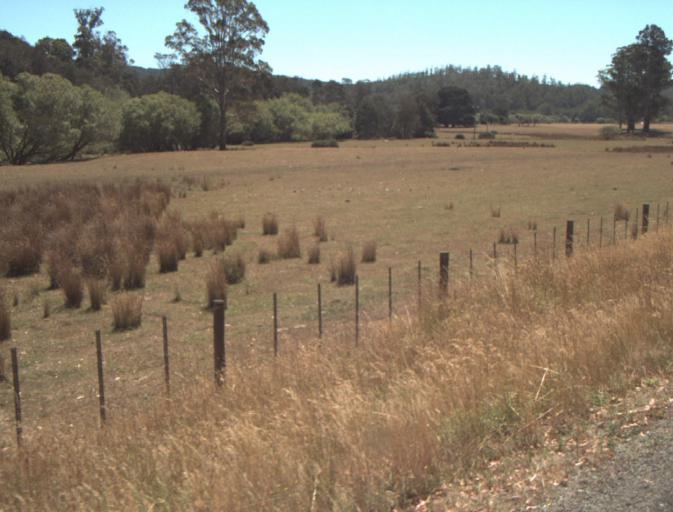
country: AU
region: Tasmania
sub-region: Dorset
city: Scottsdale
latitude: -41.2974
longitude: 147.3847
